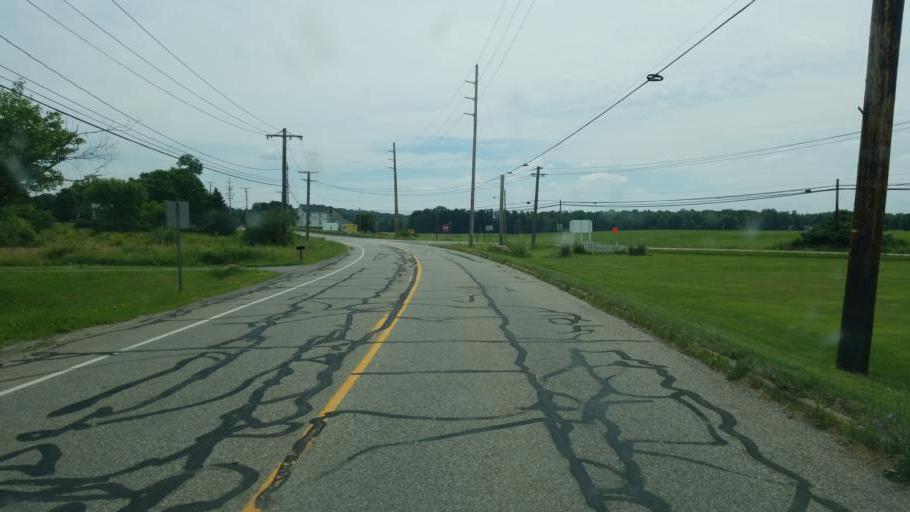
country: US
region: Ohio
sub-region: Geauga County
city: Bainbridge
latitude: 41.3888
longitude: -81.2803
